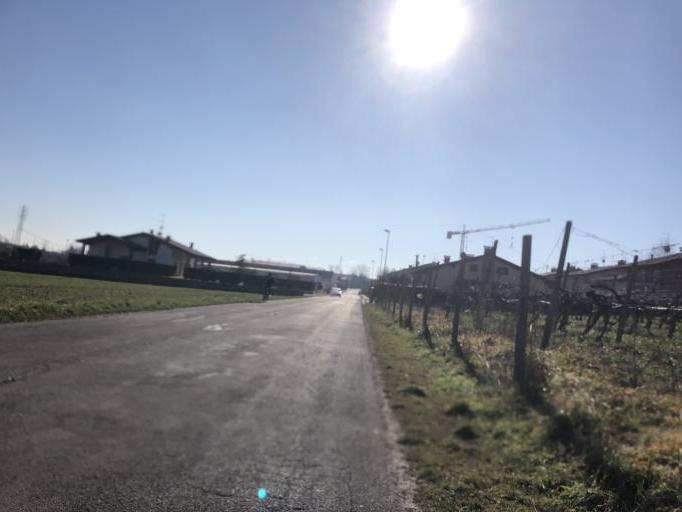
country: IT
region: Veneto
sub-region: Provincia di Verona
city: San Giorgio in Salici
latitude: 45.4281
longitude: 10.7916
